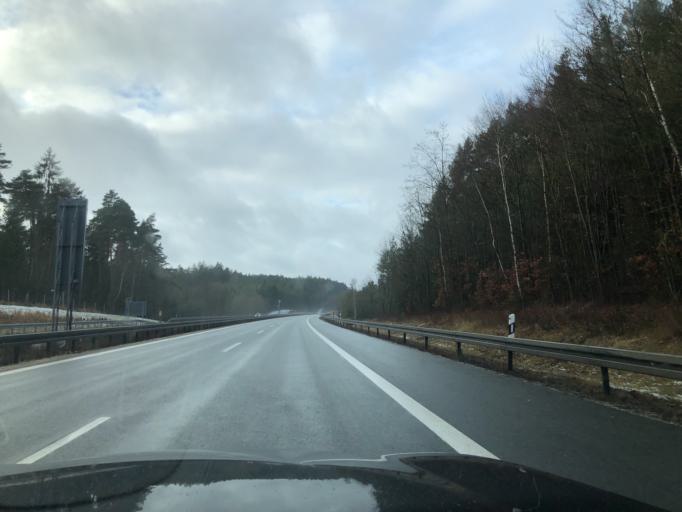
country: DE
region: Bavaria
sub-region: Upper Palatinate
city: Amberg
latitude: 49.3989
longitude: 11.8429
